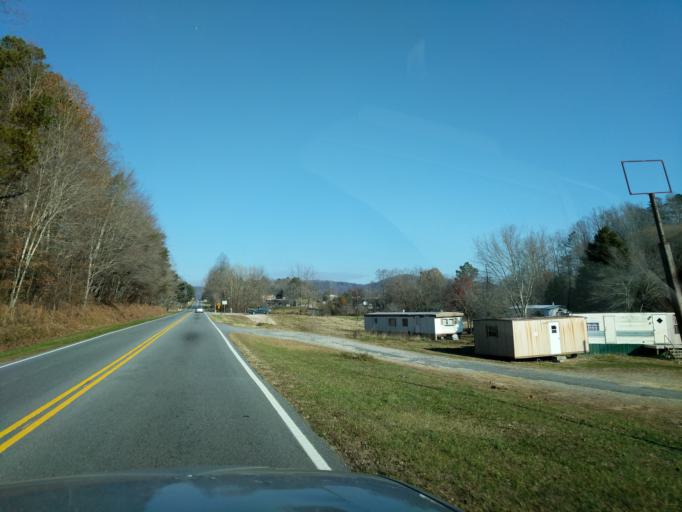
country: US
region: North Carolina
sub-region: McDowell County
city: West Marion
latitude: 35.6051
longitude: -81.9846
